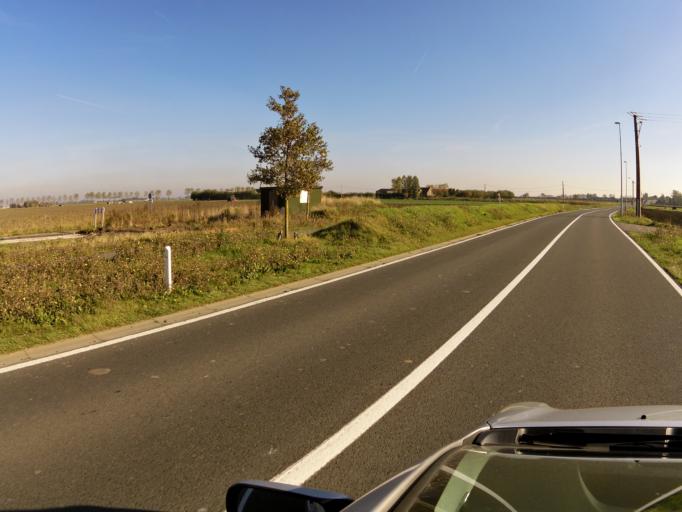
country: BE
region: Flanders
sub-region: Provincie West-Vlaanderen
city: Middelkerke
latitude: 51.1481
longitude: 2.8523
